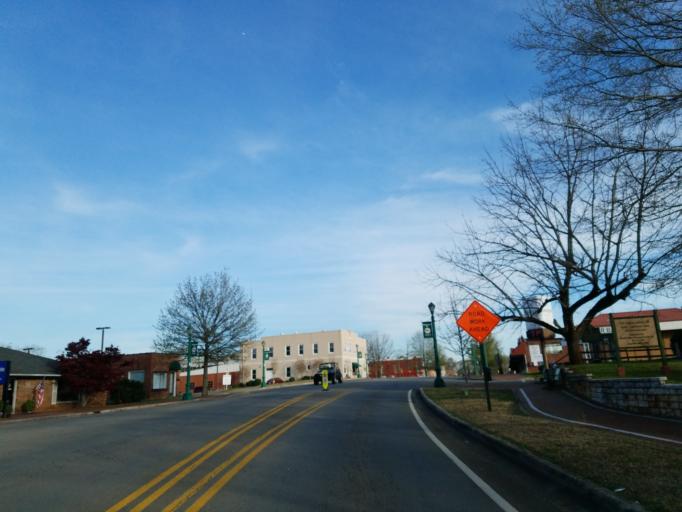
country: US
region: Georgia
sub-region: Pickens County
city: Jasper
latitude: 34.4701
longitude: -84.4313
